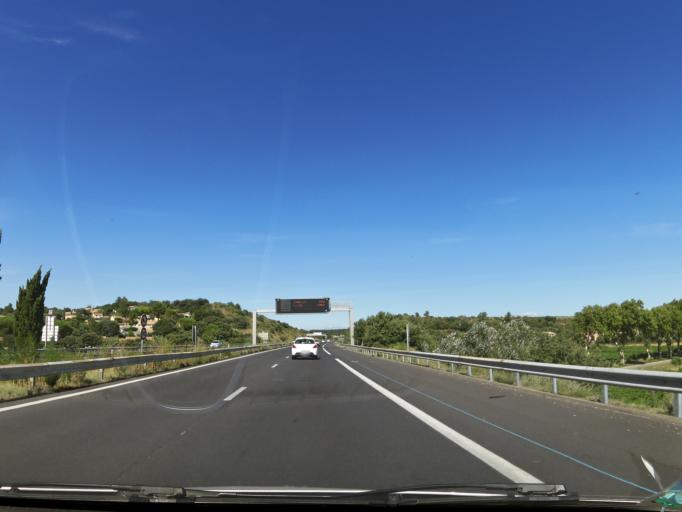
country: FR
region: Languedoc-Roussillon
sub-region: Departement du Gard
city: Tavel
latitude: 44.0094
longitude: 4.7127
